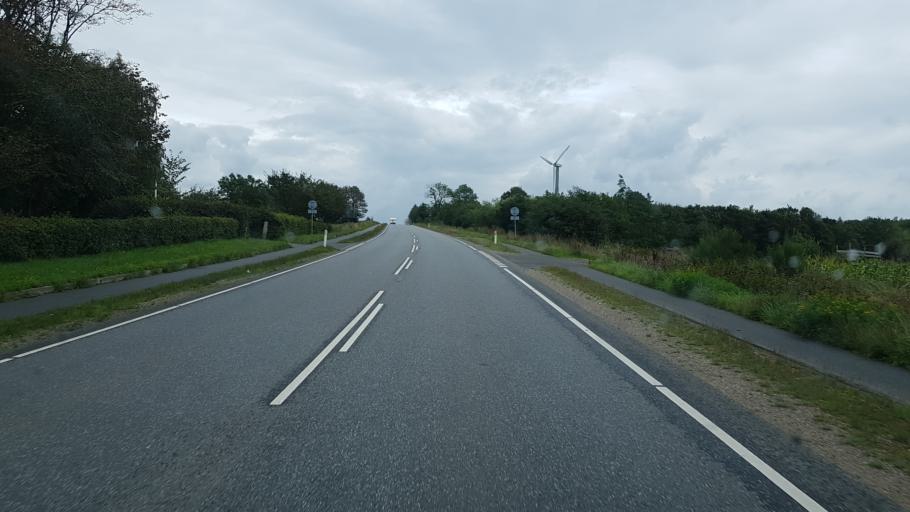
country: DK
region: Central Jutland
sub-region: Horsens Kommune
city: Braedstrup
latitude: 55.9169
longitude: 9.6996
